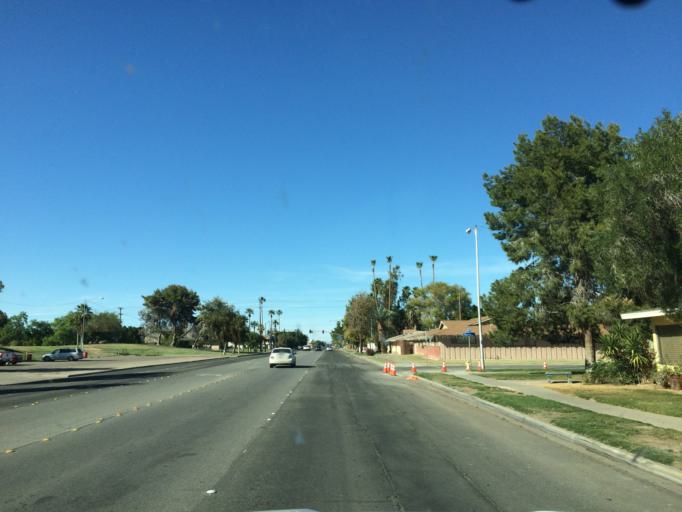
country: US
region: California
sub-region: Imperial County
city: El Centro
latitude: 32.7796
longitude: -115.5612
